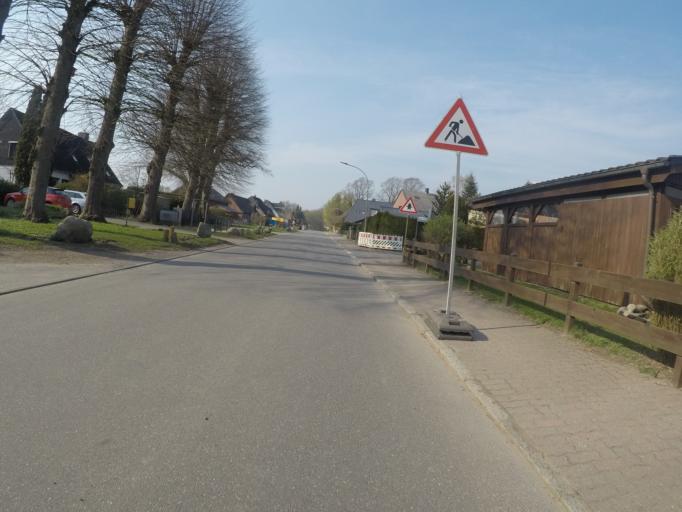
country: DE
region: Schleswig-Holstein
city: Gross Niendorf
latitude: 53.8484
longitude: 10.2444
